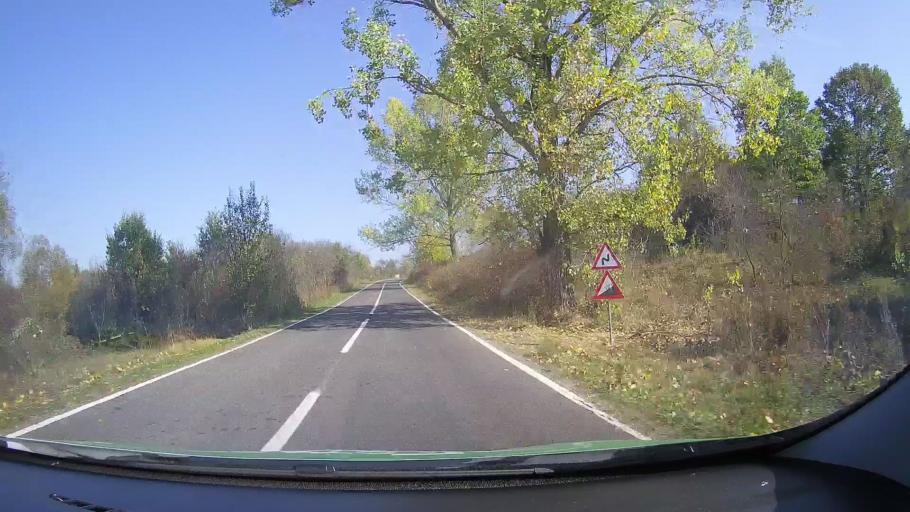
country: RO
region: Timis
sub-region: Comuna Curtea
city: Curtea
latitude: 45.8442
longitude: 22.3124
